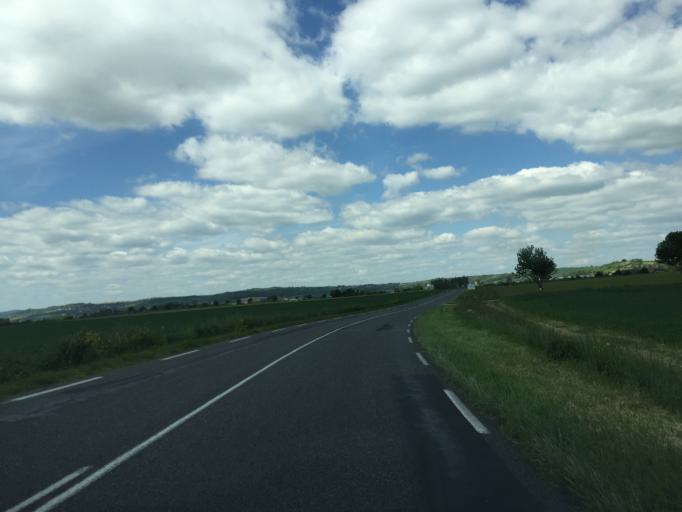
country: FR
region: Auvergne
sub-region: Departement du Puy-de-Dome
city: Aigueperse
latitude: 46.0220
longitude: 3.2259
